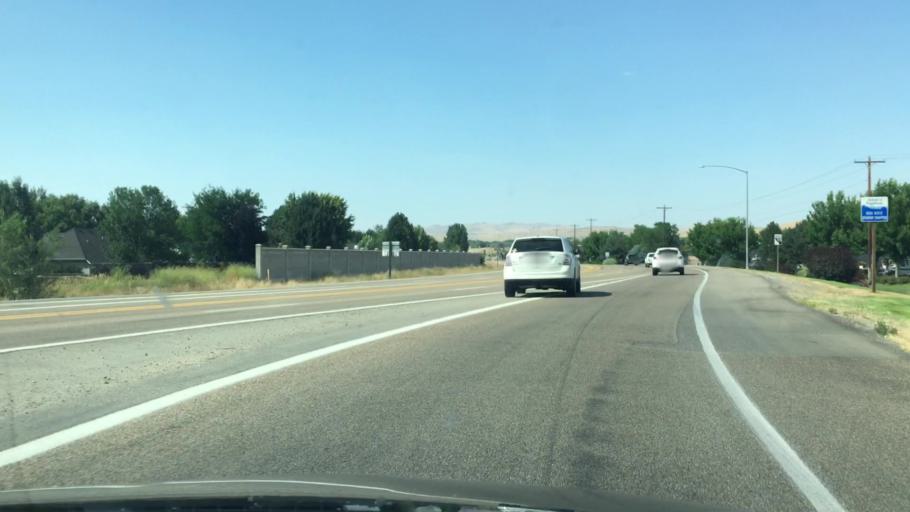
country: US
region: Idaho
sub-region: Ada County
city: Eagle
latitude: 43.6852
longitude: -116.3197
